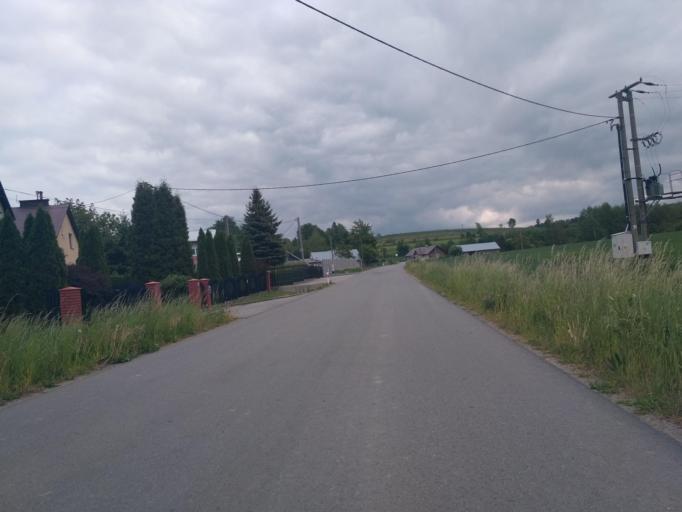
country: PL
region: Subcarpathian Voivodeship
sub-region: Powiat jasielski
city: Tarnowiec
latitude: 49.7136
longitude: 21.5868
